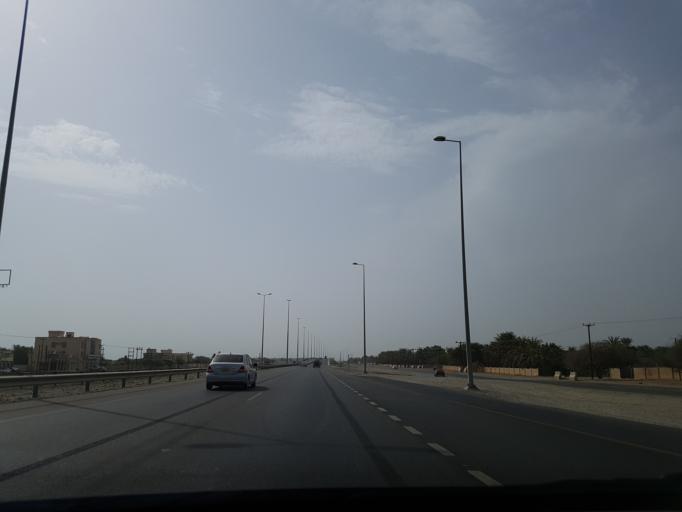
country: OM
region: Al Batinah
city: Saham
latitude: 24.1101
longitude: 56.9137
